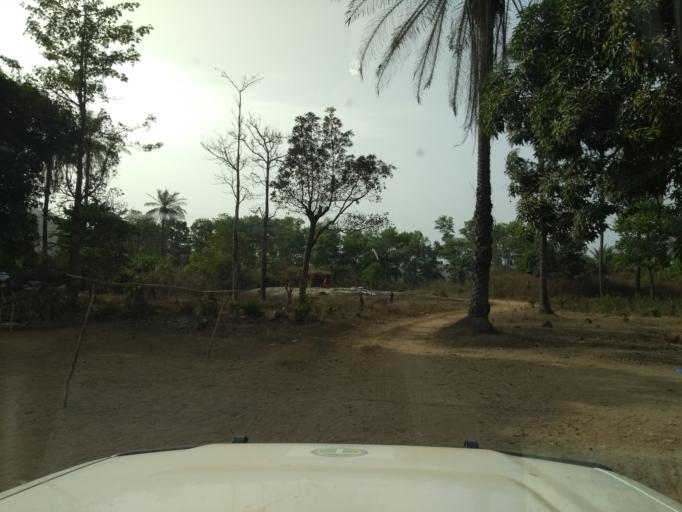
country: GN
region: Kindia
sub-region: Prefecture de Dubreka
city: Dubreka
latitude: 9.8223
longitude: -13.5552
